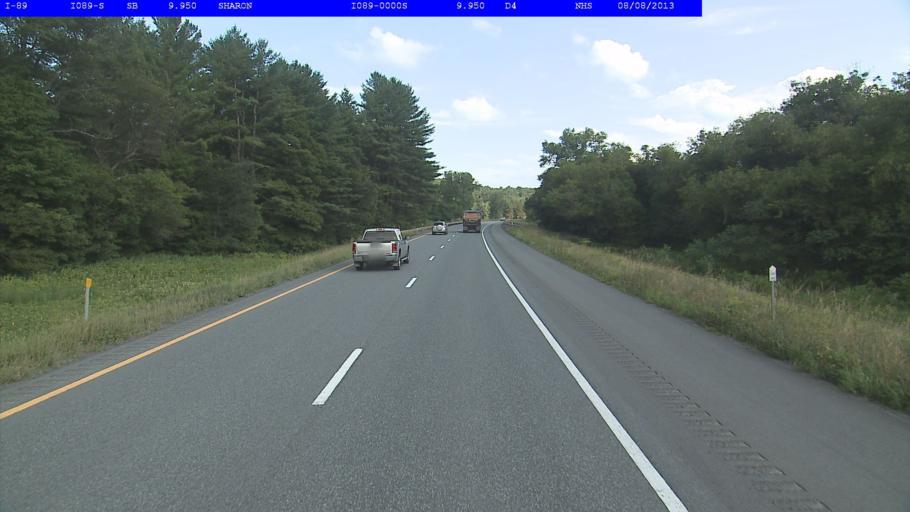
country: US
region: Vermont
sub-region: Windsor County
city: Woodstock
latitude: 43.7410
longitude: -72.4364
